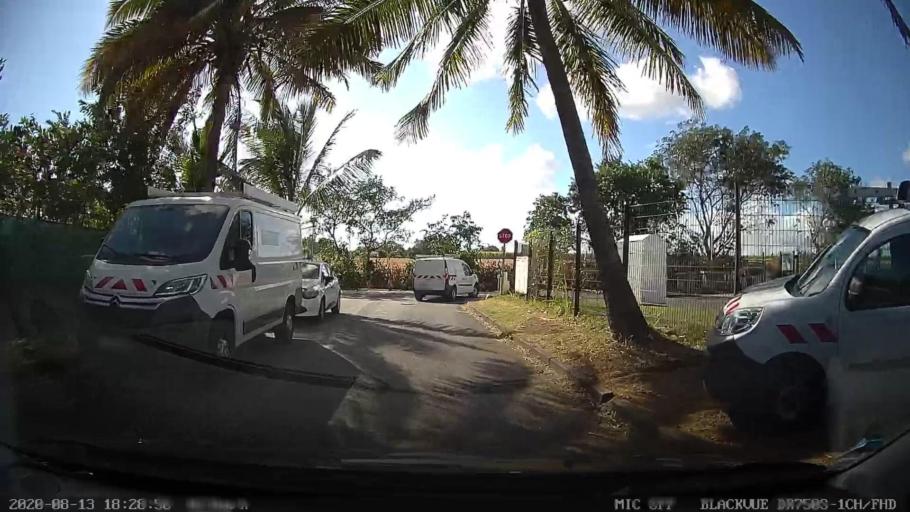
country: RE
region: Reunion
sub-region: Reunion
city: Sainte-Marie
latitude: -20.8958
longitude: 55.5367
